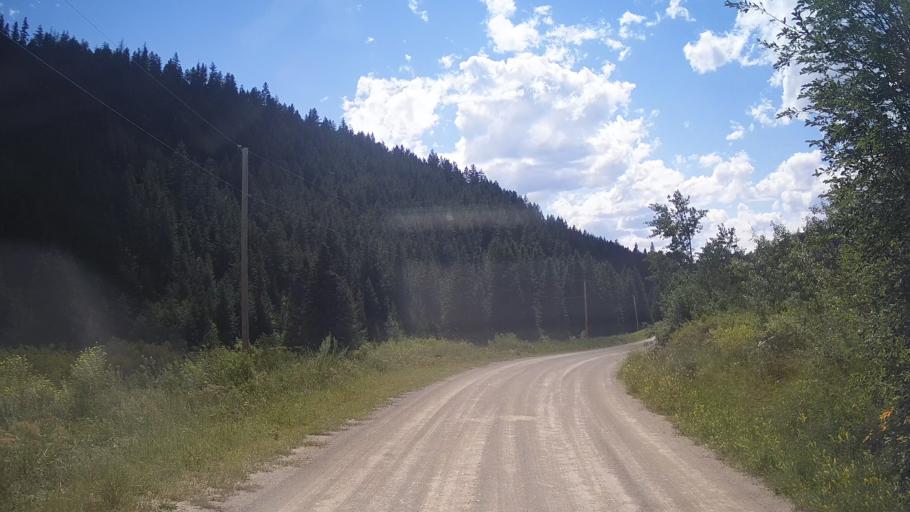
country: CA
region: British Columbia
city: Lillooet
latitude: 51.2554
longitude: -122.0053
